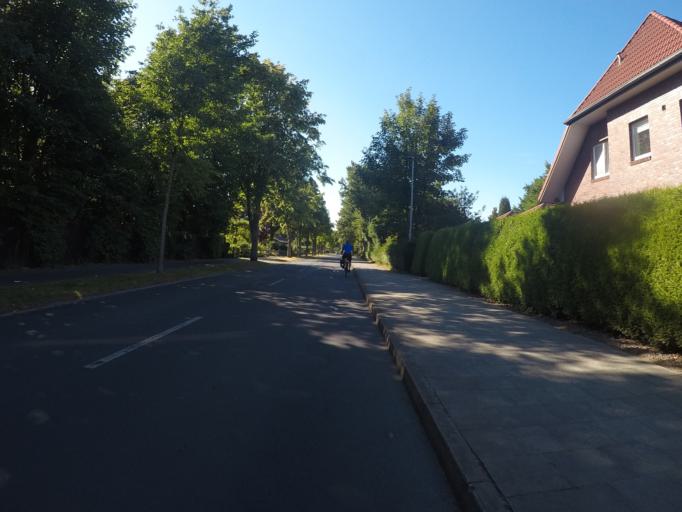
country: DE
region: Lower Saxony
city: Otterndorf
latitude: 53.8149
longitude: 8.9011
